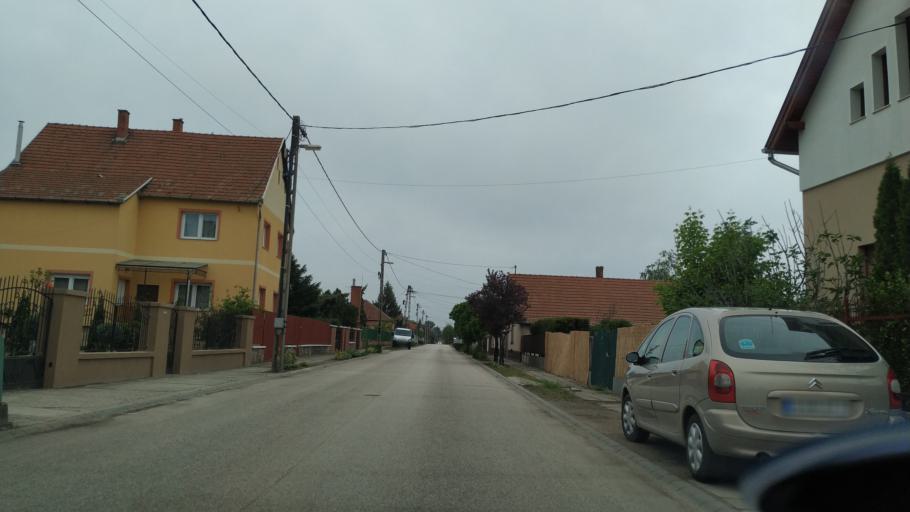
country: HU
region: Pest
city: Nagykata
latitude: 47.4096
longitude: 19.7428
